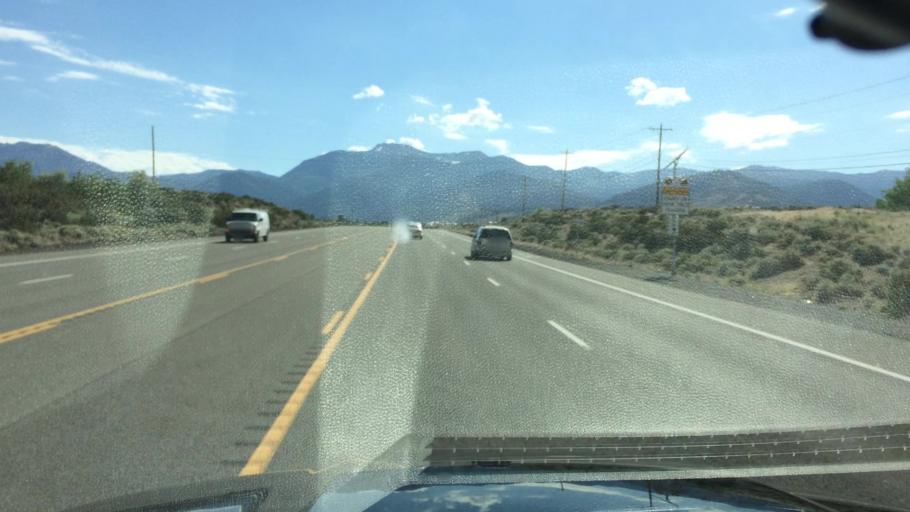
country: US
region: Nevada
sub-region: Washoe County
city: Reno
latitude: 39.3913
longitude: -119.7996
